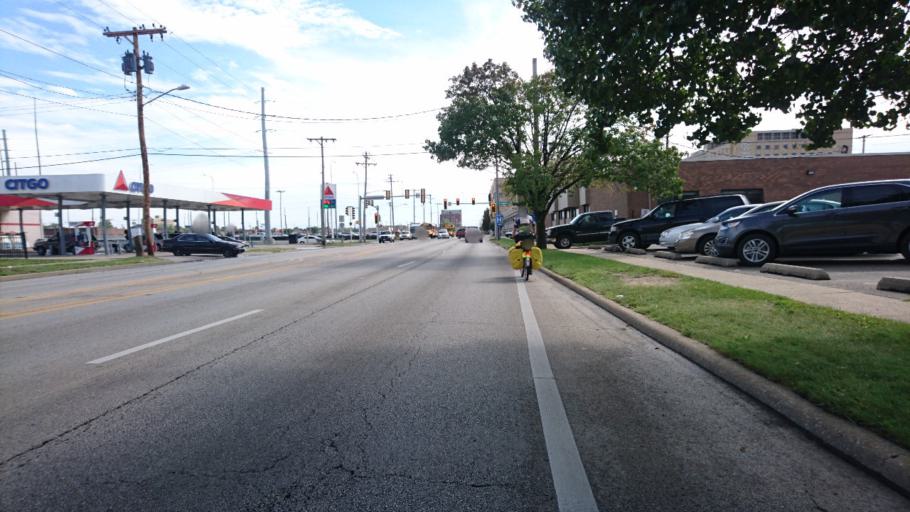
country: US
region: Illinois
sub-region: Sangamon County
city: Springfield
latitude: 39.8082
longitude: -89.6435
